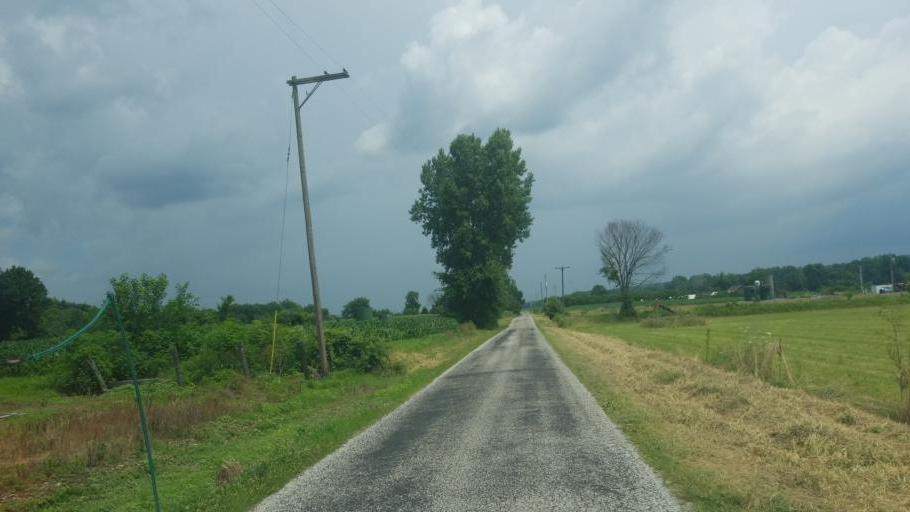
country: US
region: Ohio
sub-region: Wayne County
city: West Salem
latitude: 40.8314
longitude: -82.1430
